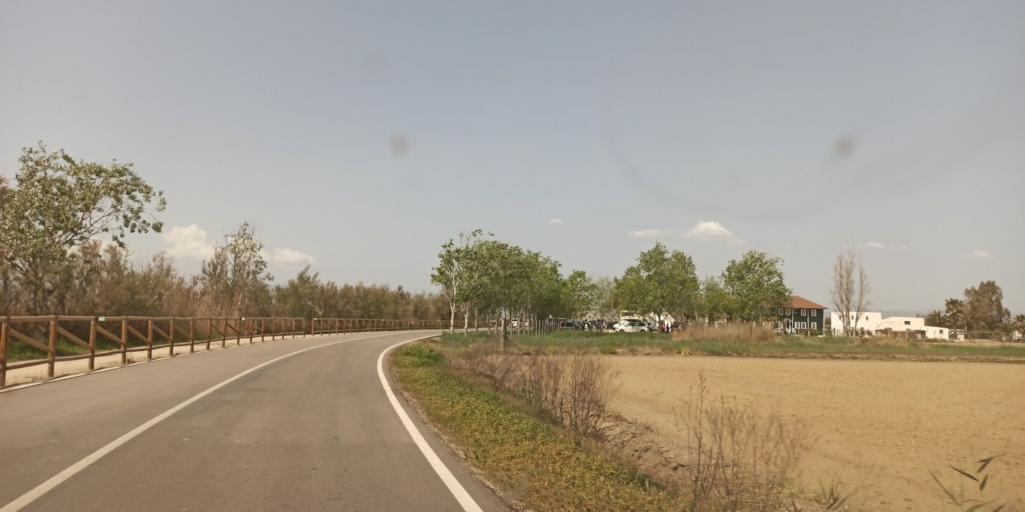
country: ES
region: Catalonia
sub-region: Provincia de Tarragona
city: Deltebre
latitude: 40.6565
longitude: 0.6765
